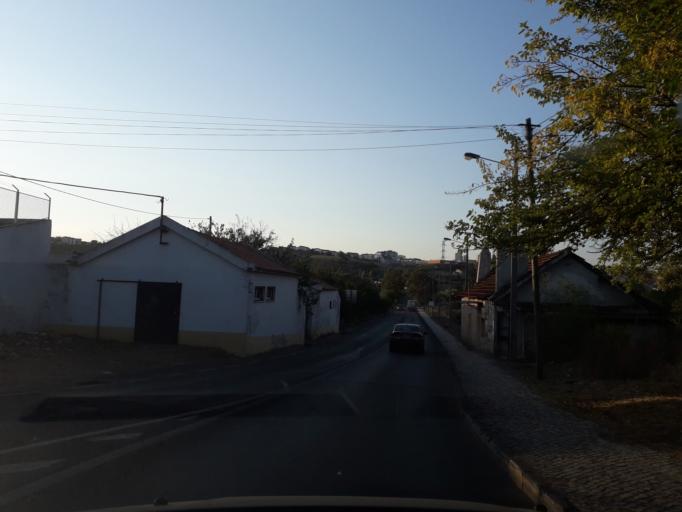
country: PT
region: Lisbon
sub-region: Odivelas
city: Pontinha
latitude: 38.7760
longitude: -9.2055
